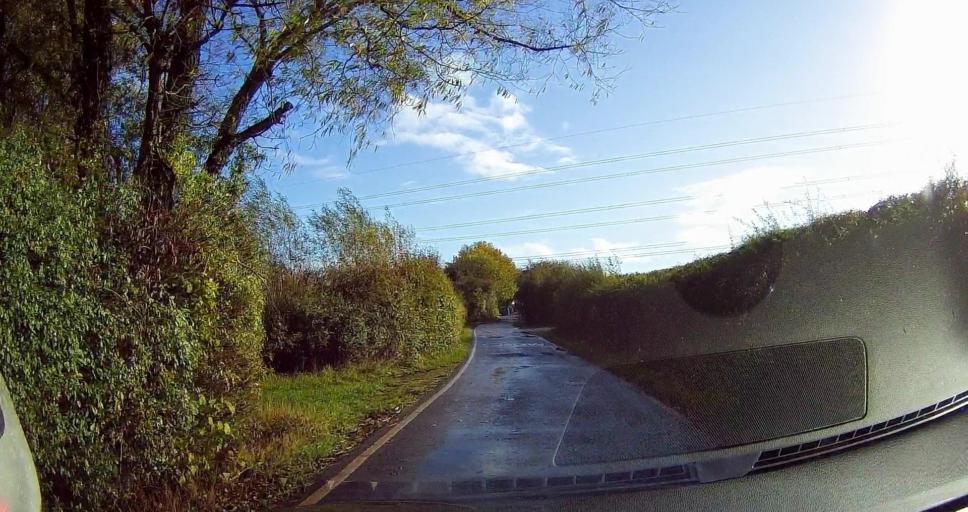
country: GB
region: England
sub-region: Staffordshire
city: Whittington
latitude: 52.6896
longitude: -1.7755
